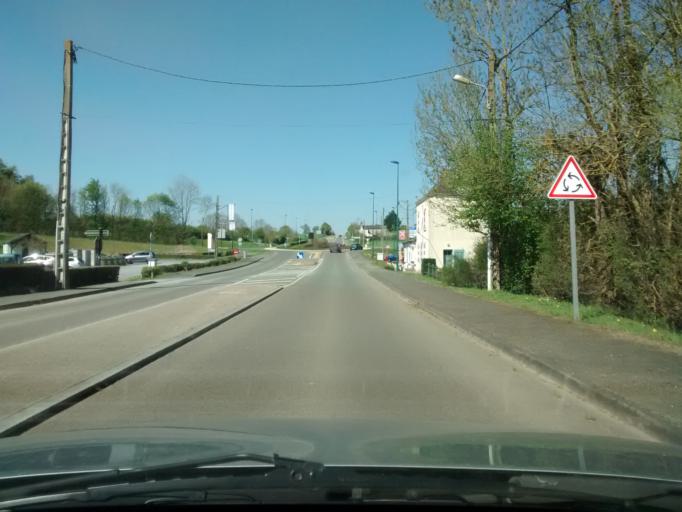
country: FR
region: Pays de la Loire
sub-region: Departement de la Mayenne
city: Vaiges
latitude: 48.0420
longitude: -0.4823
